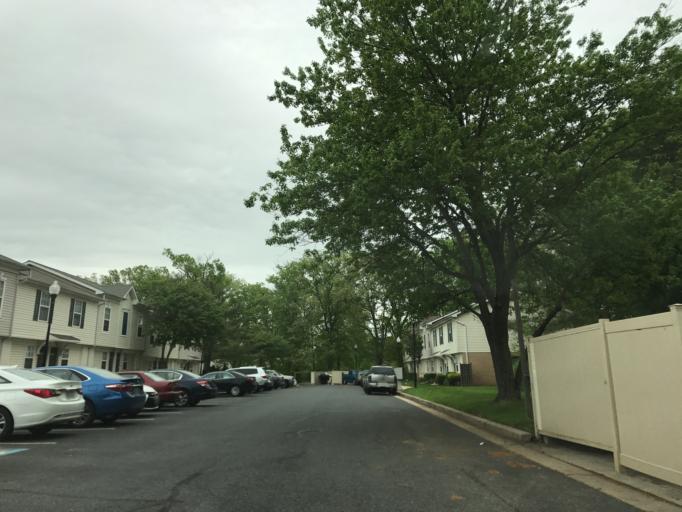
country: US
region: Maryland
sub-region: Baltimore County
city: Middle River
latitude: 39.3174
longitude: -76.4525
